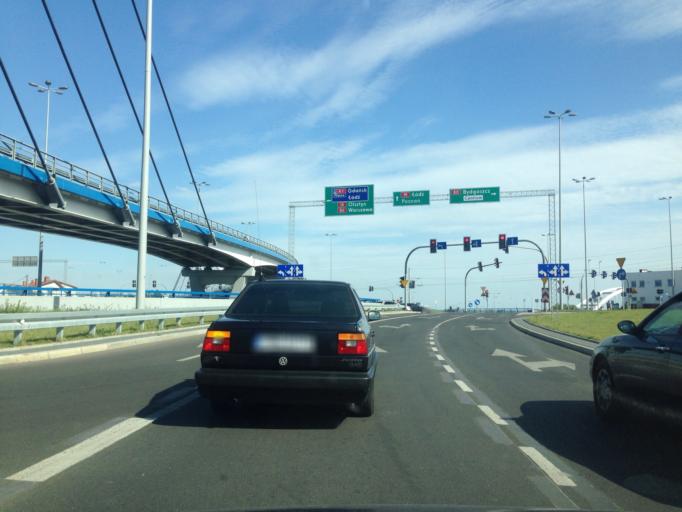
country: PL
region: Kujawsko-Pomorskie
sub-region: Torun
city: Torun
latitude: 53.0220
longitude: 18.6464
